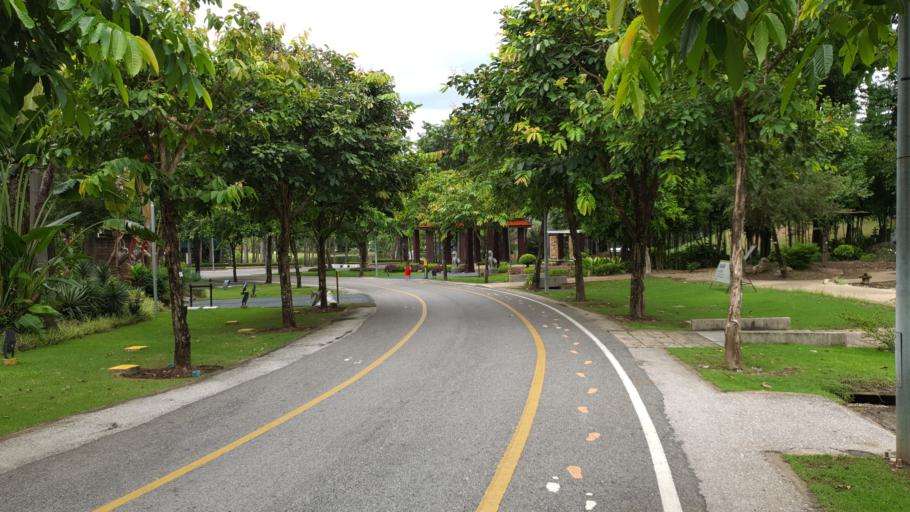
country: TH
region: Chiang Mai
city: Hang Dong
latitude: 18.7519
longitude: 98.9235
